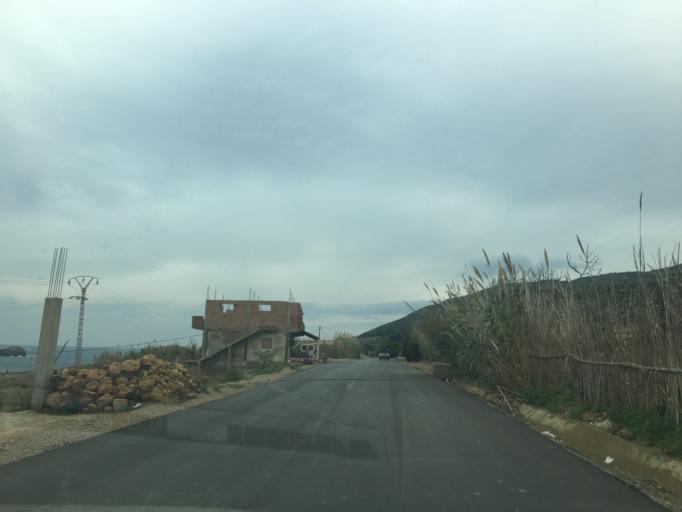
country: DZ
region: Tipaza
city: Tipasa
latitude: 36.6390
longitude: 2.3296
